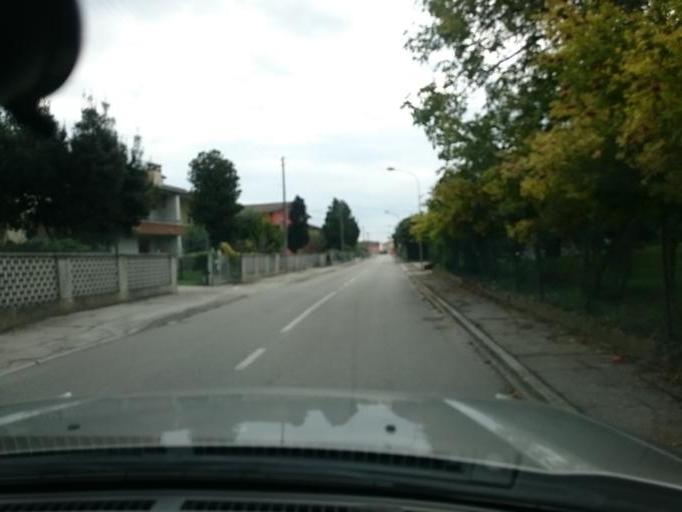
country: IT
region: Veneto
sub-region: Provincia di Padova
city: Vallonga
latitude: 45.2718
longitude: 12.0808
